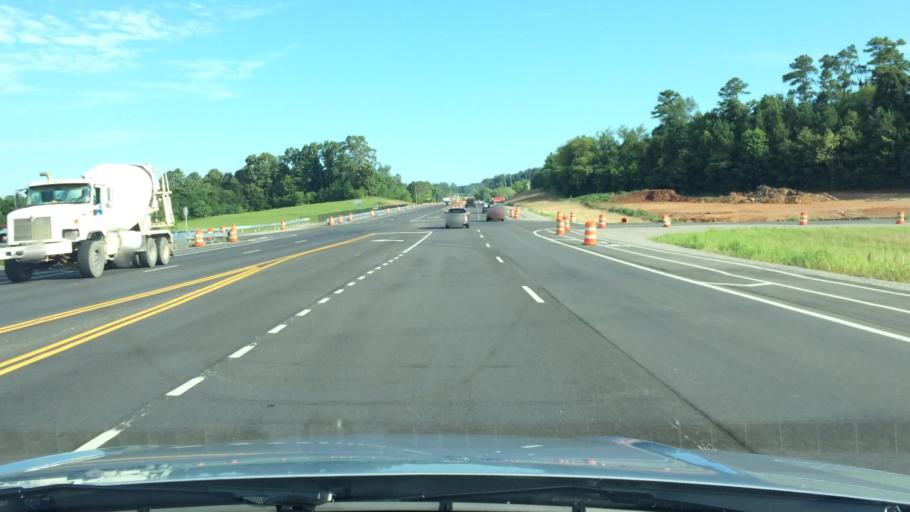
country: US
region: Tennessee
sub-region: Loudon County
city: Lenoir City
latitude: 35.7911
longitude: -84.2512
